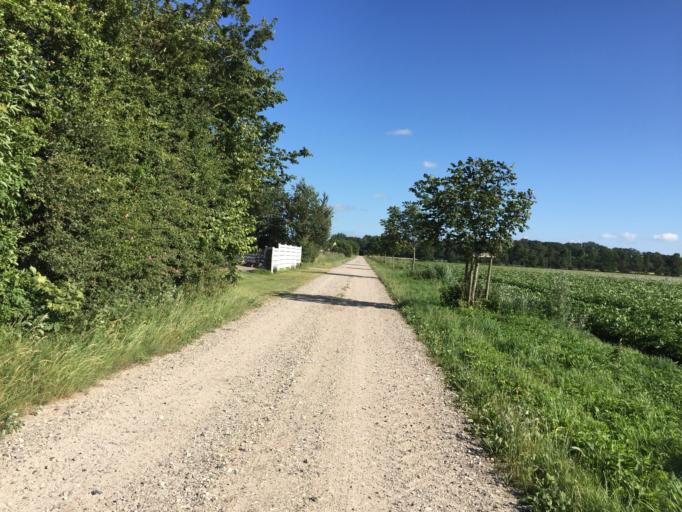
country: DK
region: South Denmark
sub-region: Kerteminde Kommune
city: Langeskov
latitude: 55.3722
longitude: 10.5436
